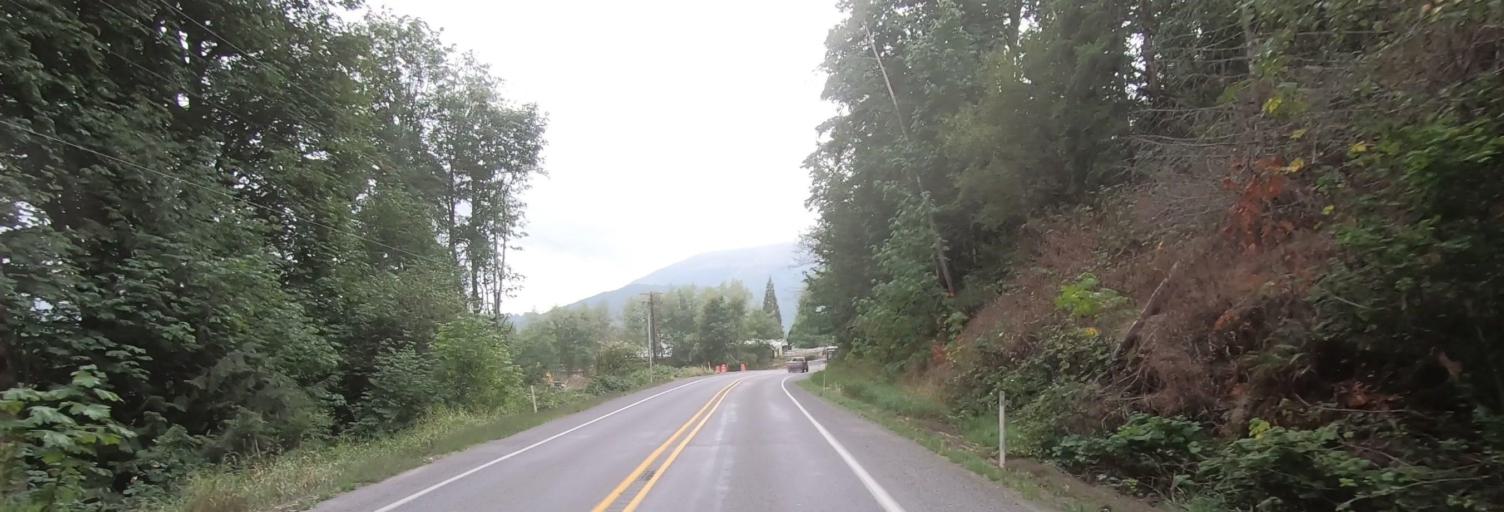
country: US
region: Washington
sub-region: Whatcom County
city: Sudden Valley
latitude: 48.6963
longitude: -122.1945
